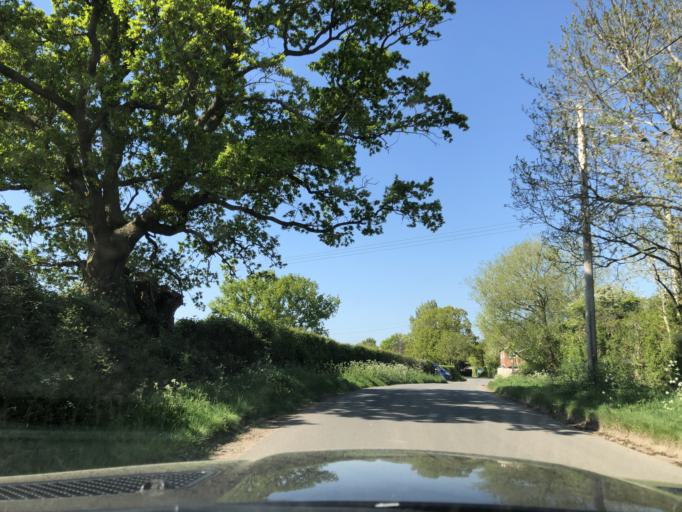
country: GB
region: England
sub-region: Warwickshire
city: Warwick
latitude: 52.2857
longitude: -1.6230
